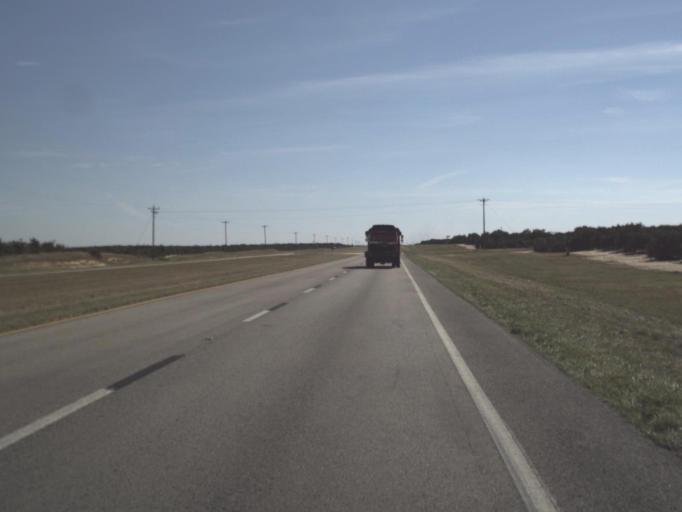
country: US
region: Florida
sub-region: Highlands County
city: Placid Lakes
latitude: 27.1552
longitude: -81.3289
